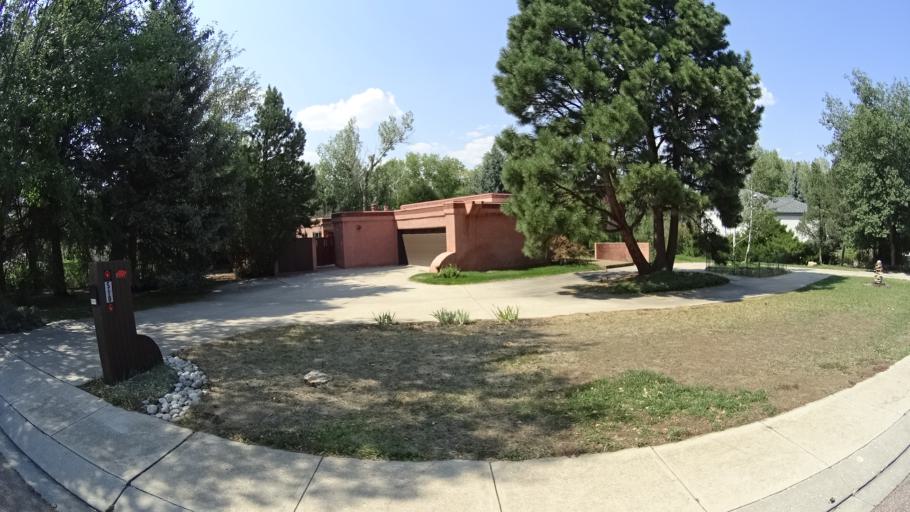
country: US
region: Colorado
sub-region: El Paso County
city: Colorado Springs
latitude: 38.8004
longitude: -104.8370
